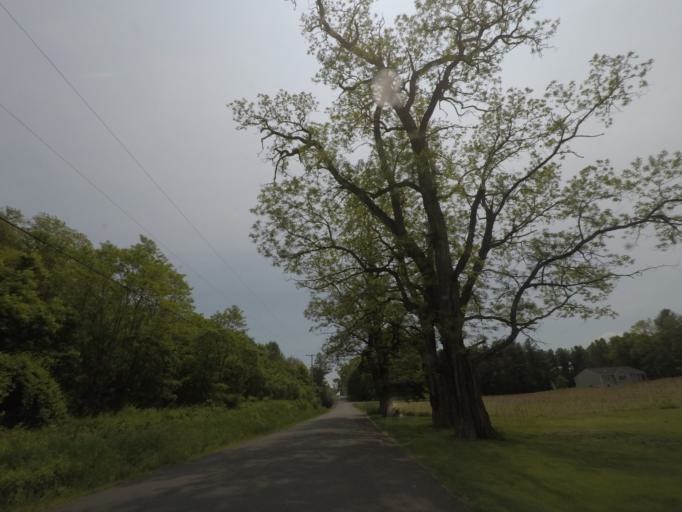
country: US
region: New York
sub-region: Rensselaer County
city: East Greenbush
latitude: 42.5453
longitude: -73.6937
